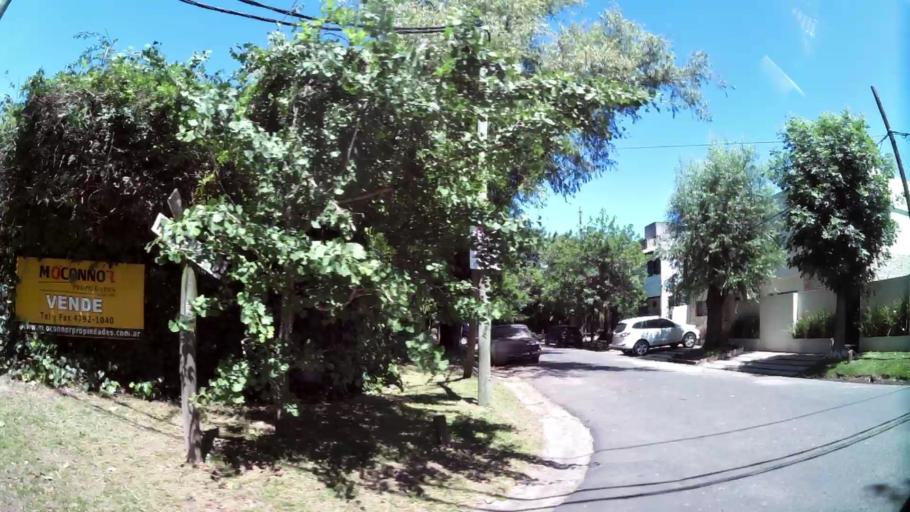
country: AR
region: Buenos Aires
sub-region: Partido de San Isidro
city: San Isidro
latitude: -34.4585
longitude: -58.5101
